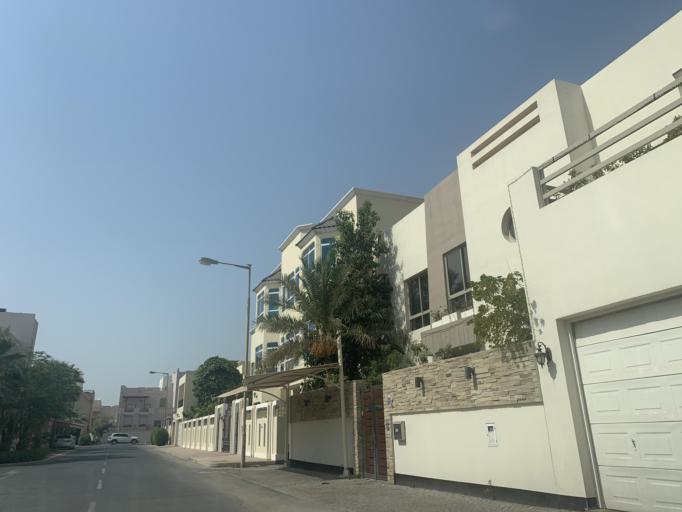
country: BH
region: Manama
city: Jidd Hafs
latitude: 26.2060
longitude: 50.4933
